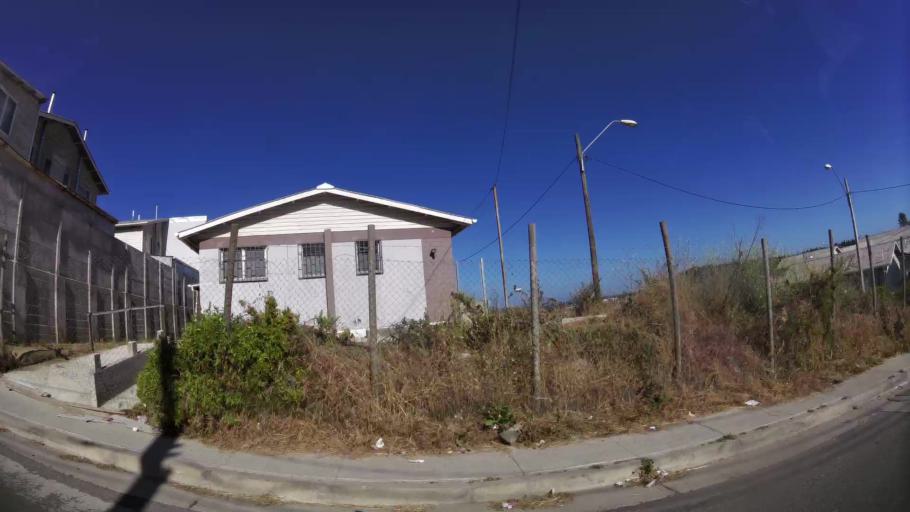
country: CL
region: Valparaiso
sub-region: Provincia de Valparaiso
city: Valparaiso
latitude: -33.1193
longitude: -71.5839
